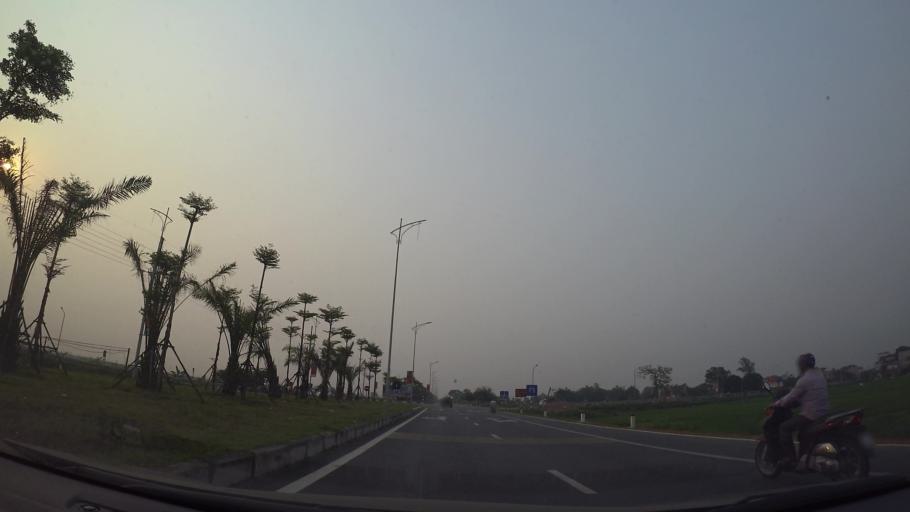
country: VN
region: Ha Noi
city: Kim Bai
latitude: 20.8910
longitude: 105.7947
